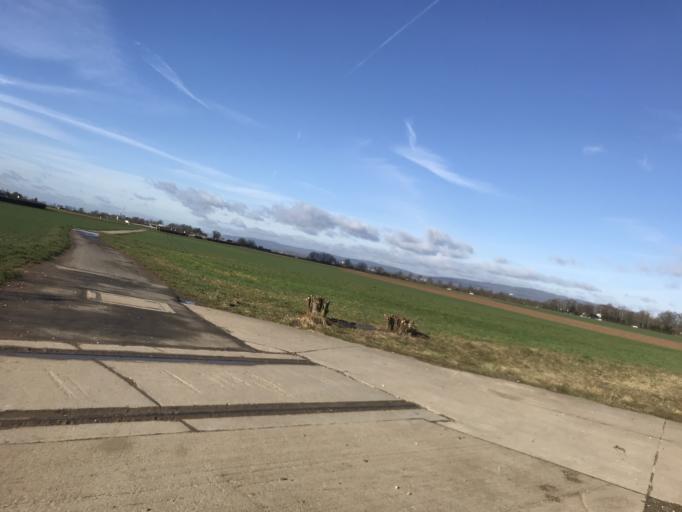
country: DE
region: Hesse
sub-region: Regierungsbezirk Darmstadt
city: Hochheim am Main
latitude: 50.0452
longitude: 8.3102
